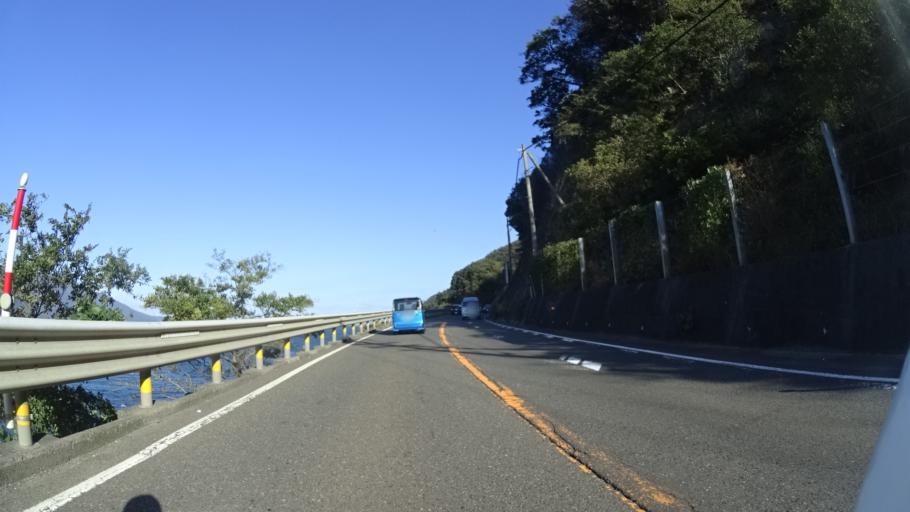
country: JP
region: Fukui
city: Tsuruga
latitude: 35.6903
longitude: 136.0815
